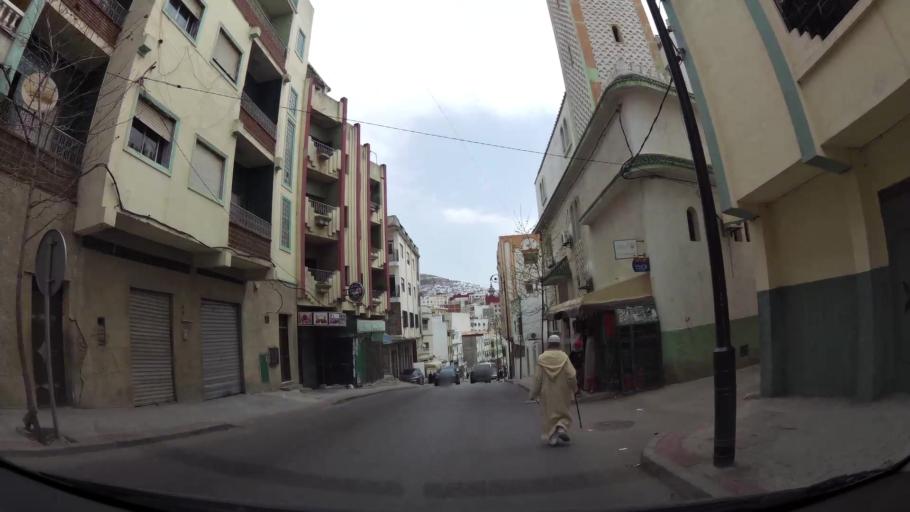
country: MA
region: Tanger-Tetouan
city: Tetouan
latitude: 35.5667
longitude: -5.3945
